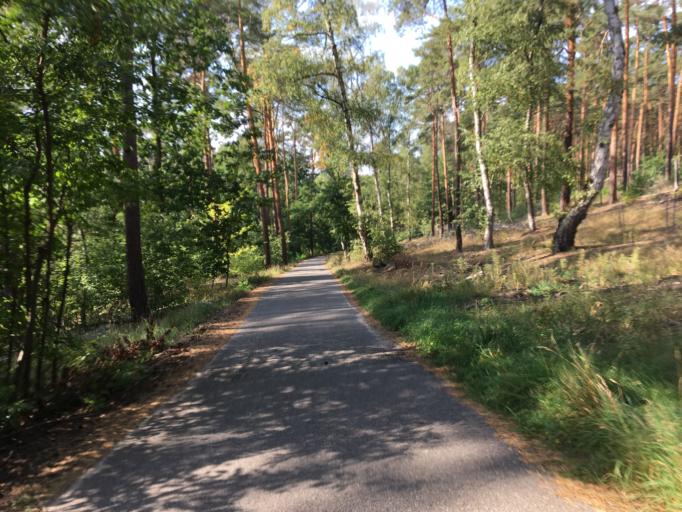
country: DE
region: Berlin
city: Muggelheim
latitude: 52.4097
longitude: 13.6424
